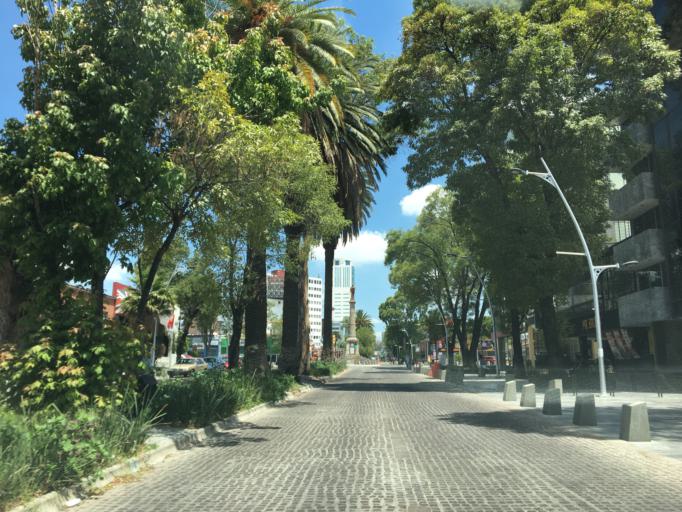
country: MX
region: Puebla
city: Puebla
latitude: 19.0510
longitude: -98.2170
